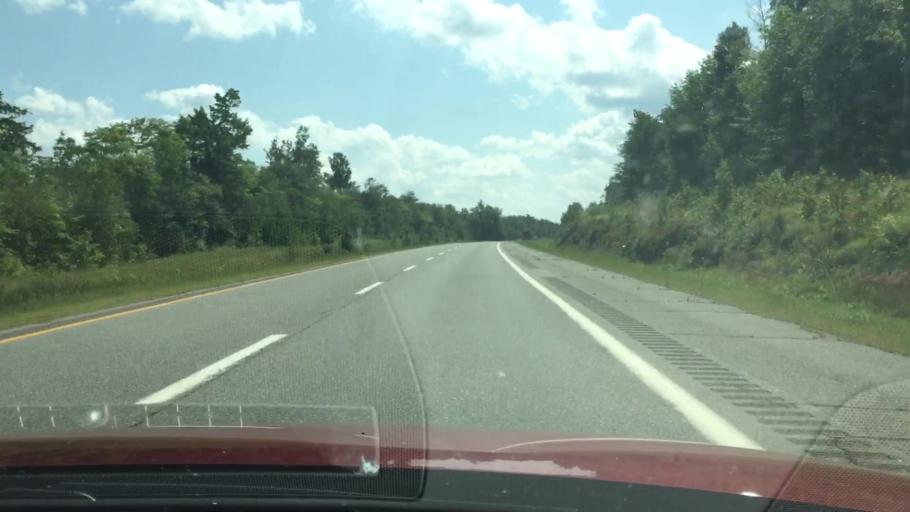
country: US
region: Maine
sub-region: Penobscot County
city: Lincoln
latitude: 45.4301
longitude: -68.5894
